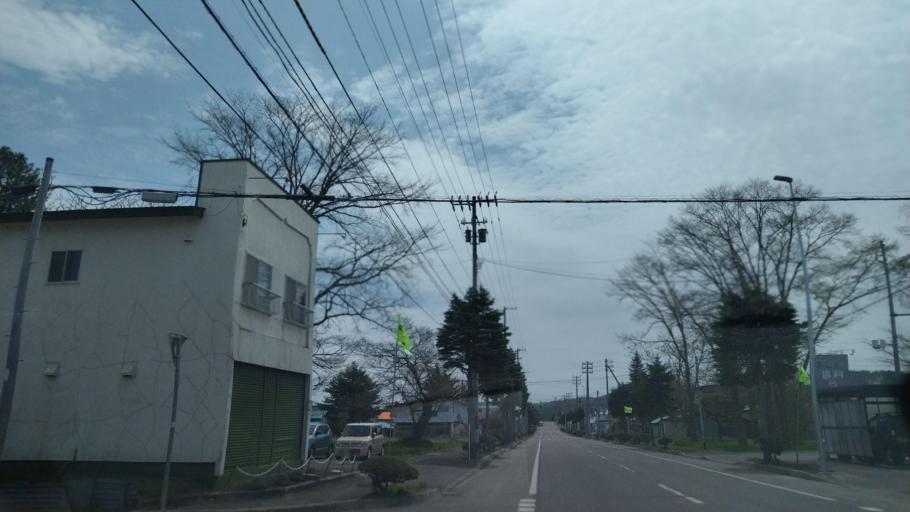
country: JP
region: Hokkaido
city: Otofuke
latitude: 43.2417
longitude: 143.5525
